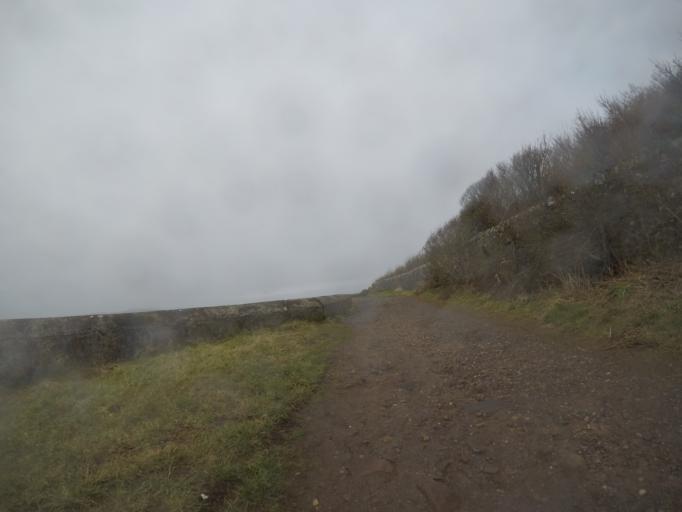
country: GB
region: Scotland
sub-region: North Ayrshire
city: Millport
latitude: 55.7008
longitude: -4.9044
